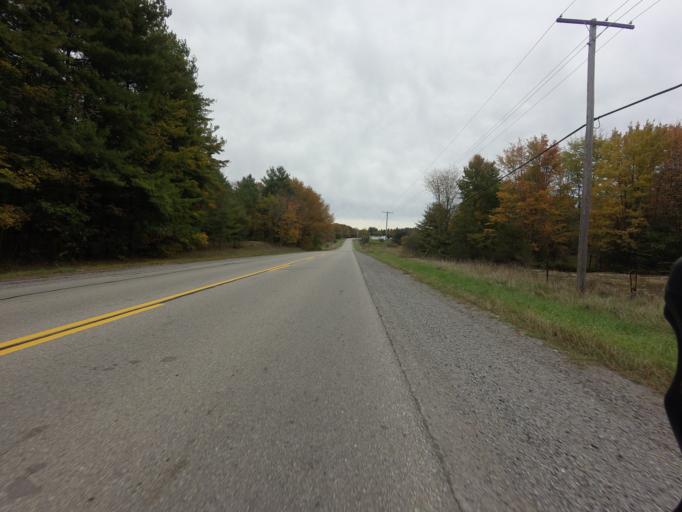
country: CA
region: Ontario
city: Gananoque
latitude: 44.5580
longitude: -76.1176
